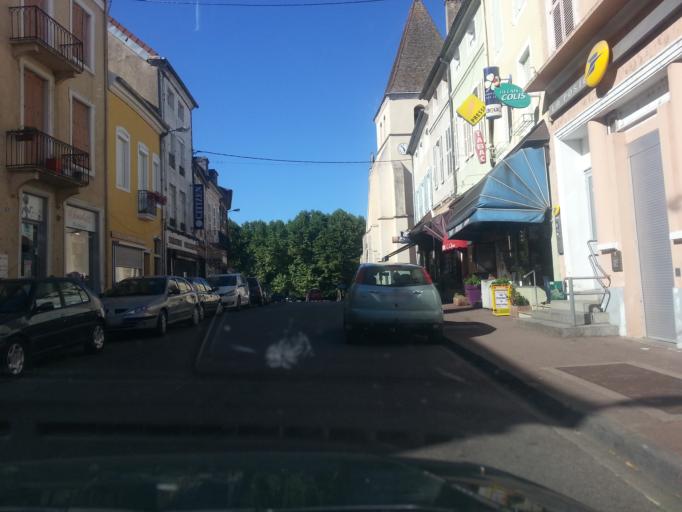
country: FR
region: Bourgogne
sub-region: Departement de Saone-et-Loire
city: Verdun-sur-le-Doubs
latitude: 46.8956
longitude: 5.0243
